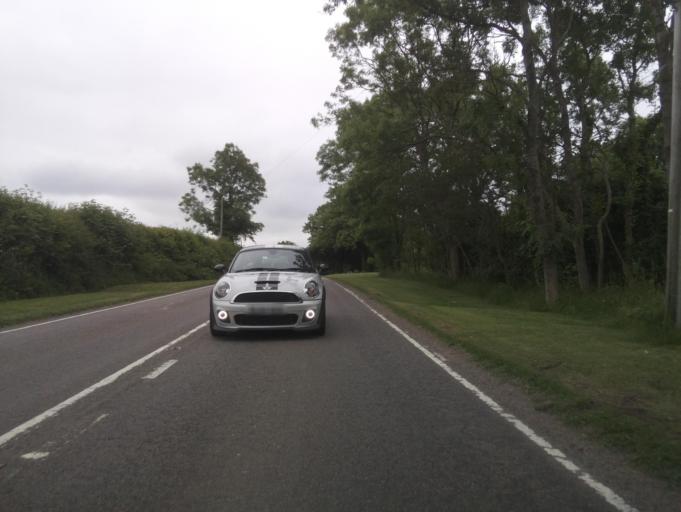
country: GB
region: England
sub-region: Leicestershire
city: Barrow upon Soar
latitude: 52.8091
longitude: -1.1191
